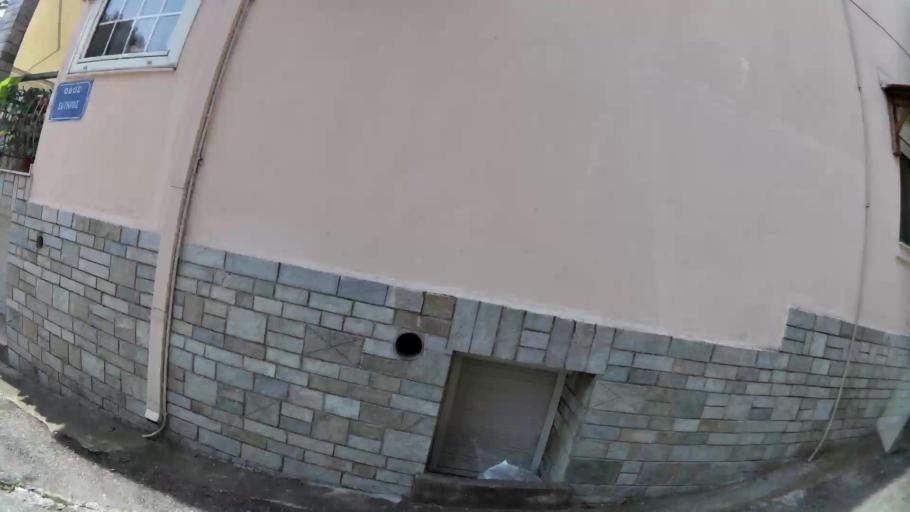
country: GR
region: Central Macedonia
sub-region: Nomos Thessalonikis
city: Stavroupoli
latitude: 40.6735
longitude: 22.9372
